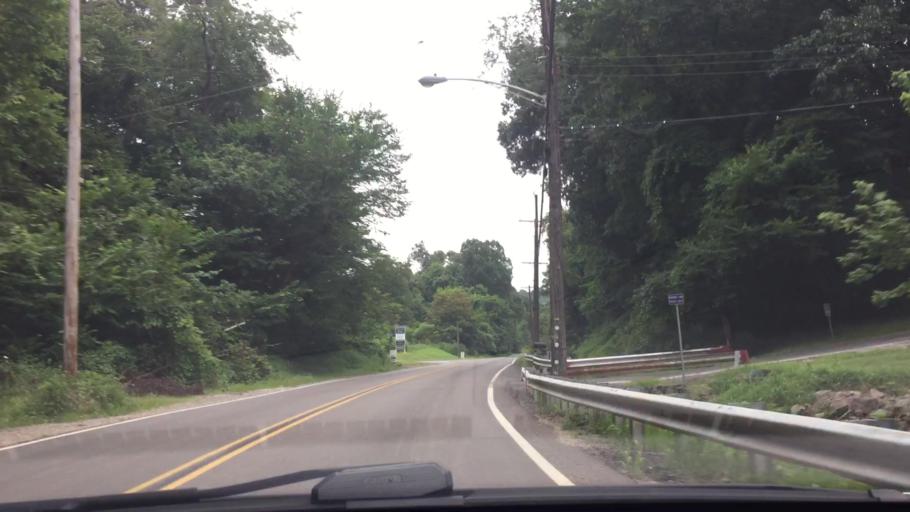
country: US
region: Pennsylvania
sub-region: Allegheny County
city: Rennerdale
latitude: 40.3902
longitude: -80.1585
